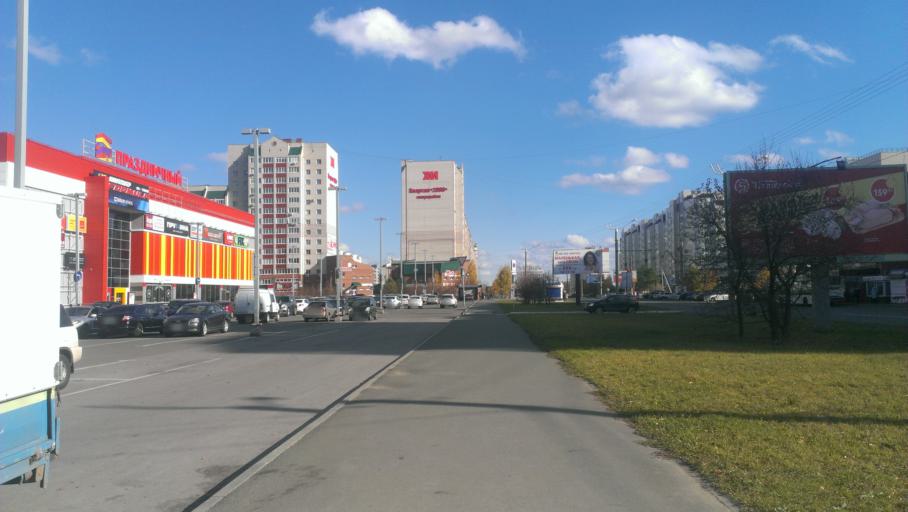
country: RU
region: Altai Krai
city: Novosilikatnyy
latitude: 53.3350
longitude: 83.6827
